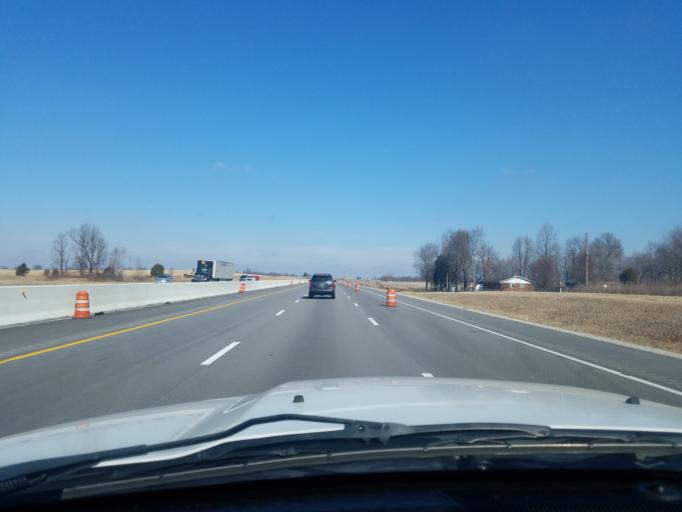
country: US
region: Kentucky
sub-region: Larue County
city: Hodgenville
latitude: 37.5443
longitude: -85.8799
